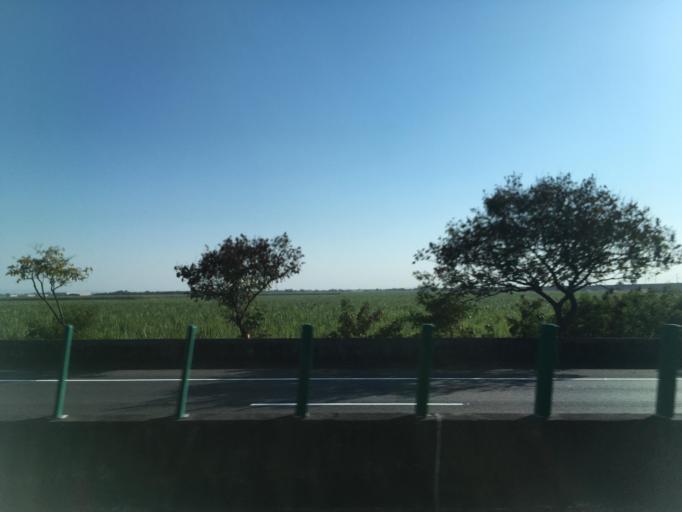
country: TW
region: Taiwan
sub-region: Chiayi
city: Taibao
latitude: 23.4287
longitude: 120.3254
